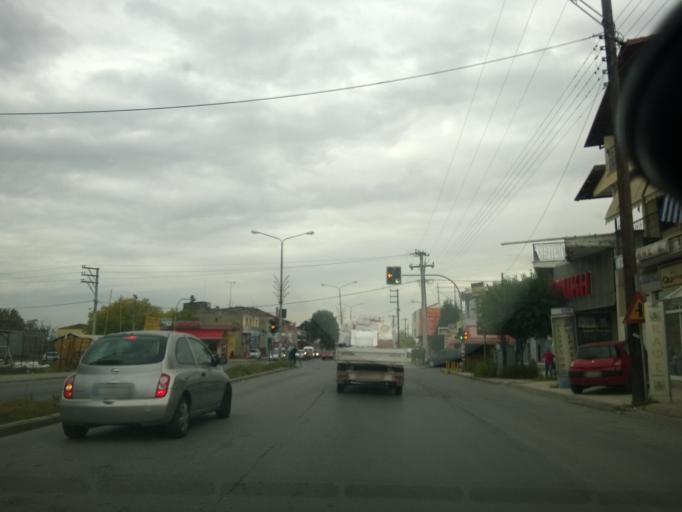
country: GR
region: Central Macedonia
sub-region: Nomos Pellis
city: Giannitsa
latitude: 40.7847
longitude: 22.4051
